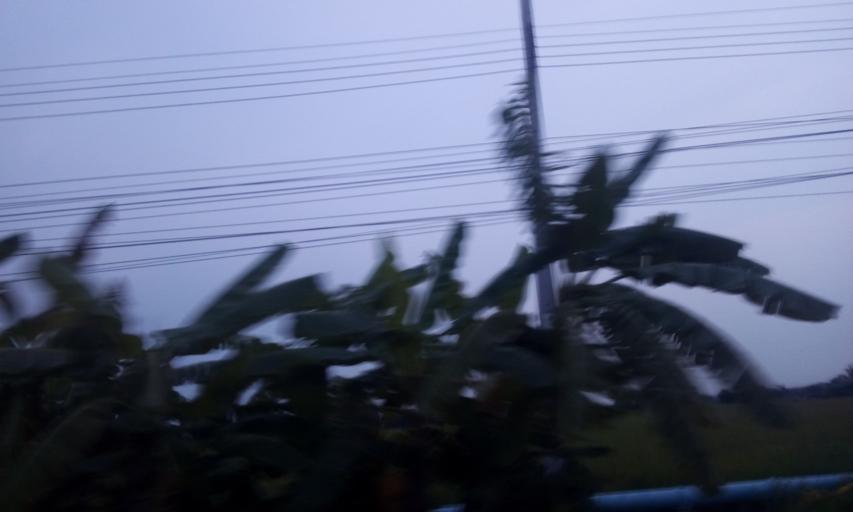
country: TH
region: Bangkok
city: Nong Chok
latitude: 13.8221
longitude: 100.9255
